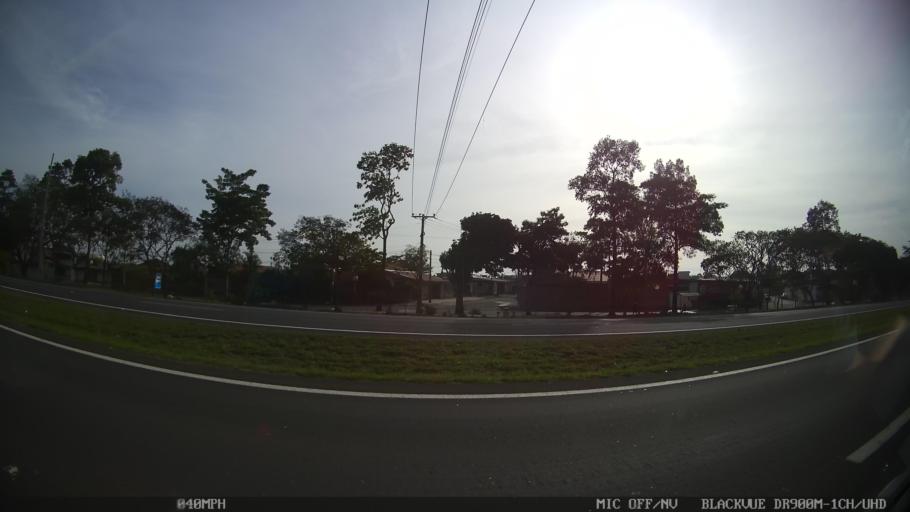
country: BR
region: Sao Paulo
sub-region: Piracicaba
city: Piracicaba
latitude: -22.6791
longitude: -47.7099
